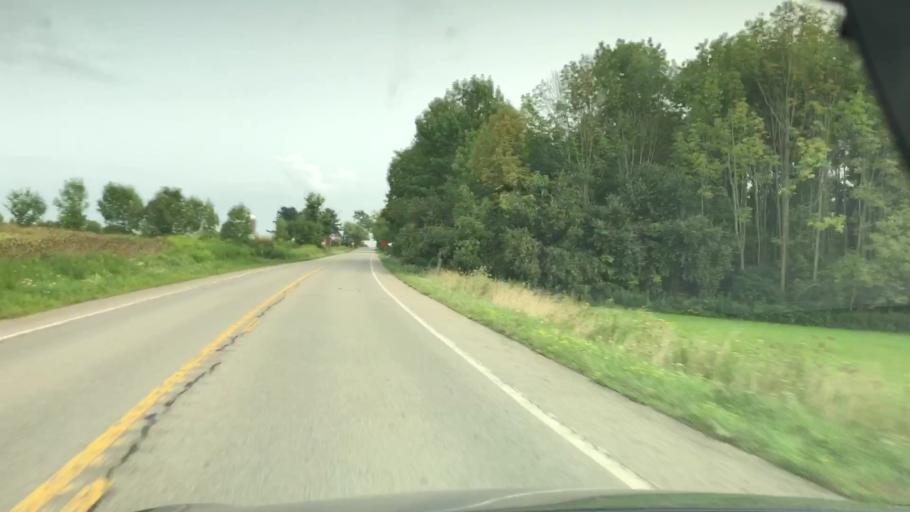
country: US
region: Pennsylvania
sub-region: Erie County
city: Union City
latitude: 41.8139
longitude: -79.8030
